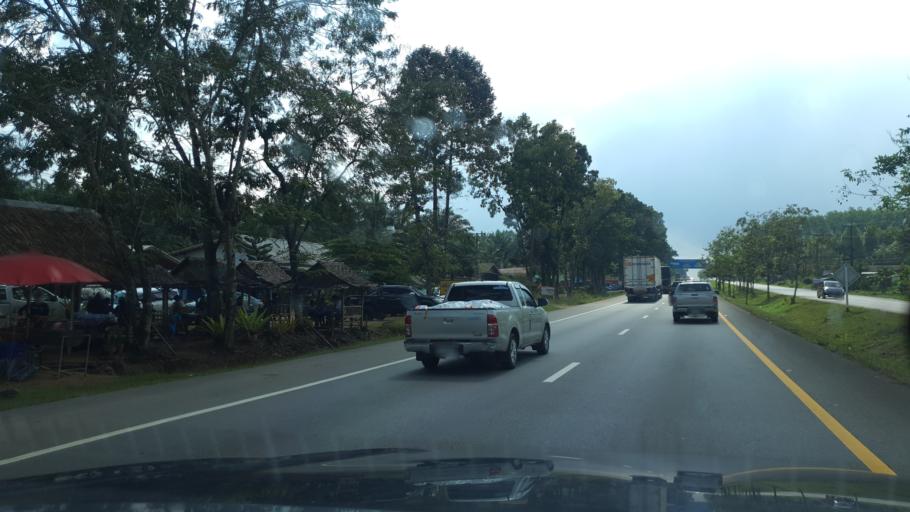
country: TH
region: Chumphon
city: Tha Sae
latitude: 10.7740
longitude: 99.1932
